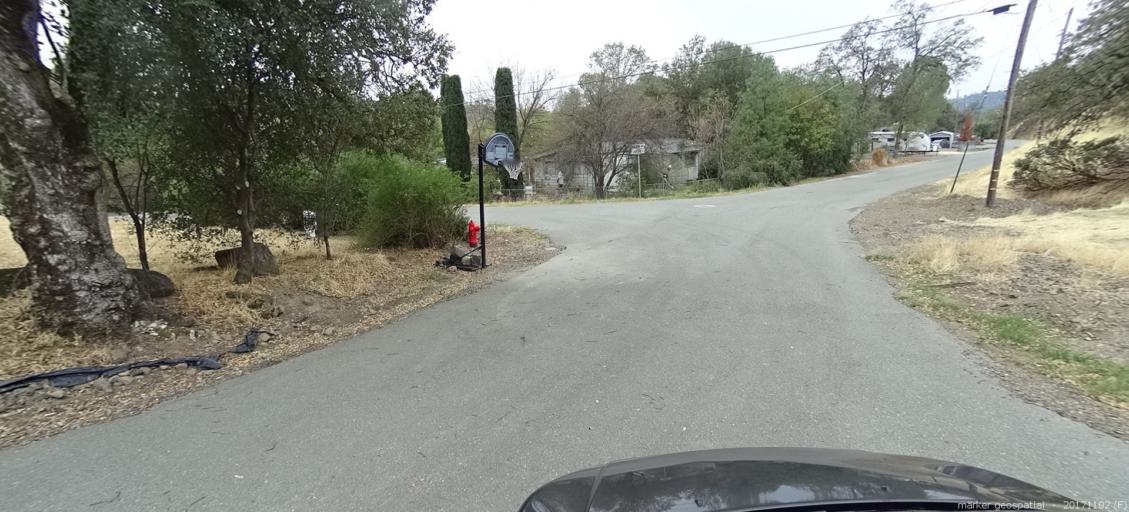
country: US
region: California
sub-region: Shasta County
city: Bella Vista
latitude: 40.7201
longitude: -122.2339
